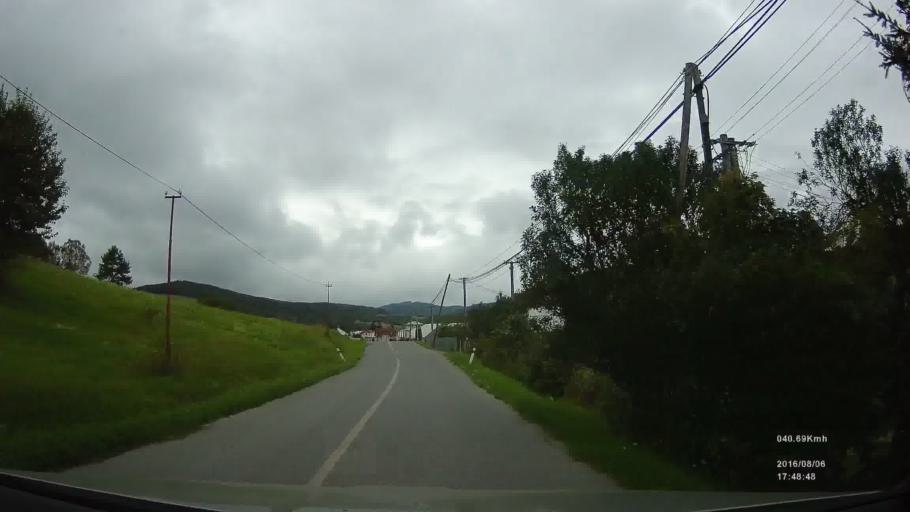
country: SK
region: Presovsky
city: Svidnik
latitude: 49.3791
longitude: 21.5726
